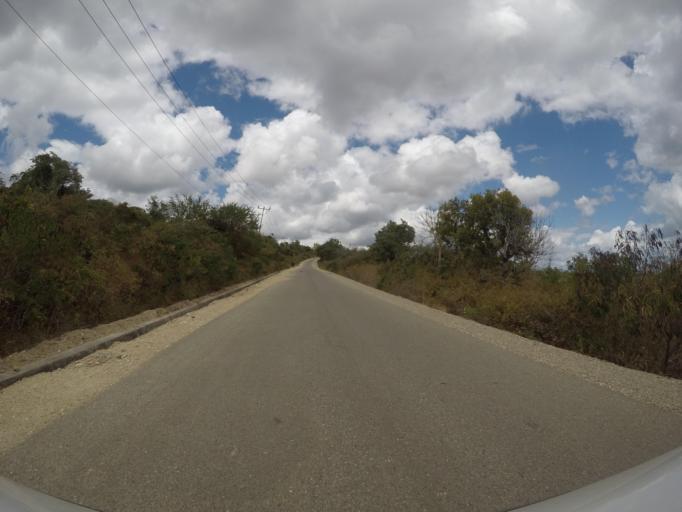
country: TL
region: Lautem
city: Lospalos
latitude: -8.3658
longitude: 126.9285
